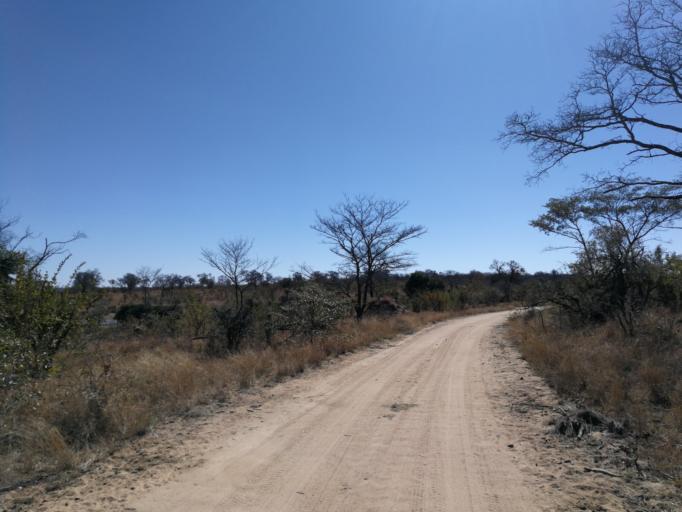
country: ZA
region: Limpopo
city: Thulamahashi
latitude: -24.8576
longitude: 31.7537
